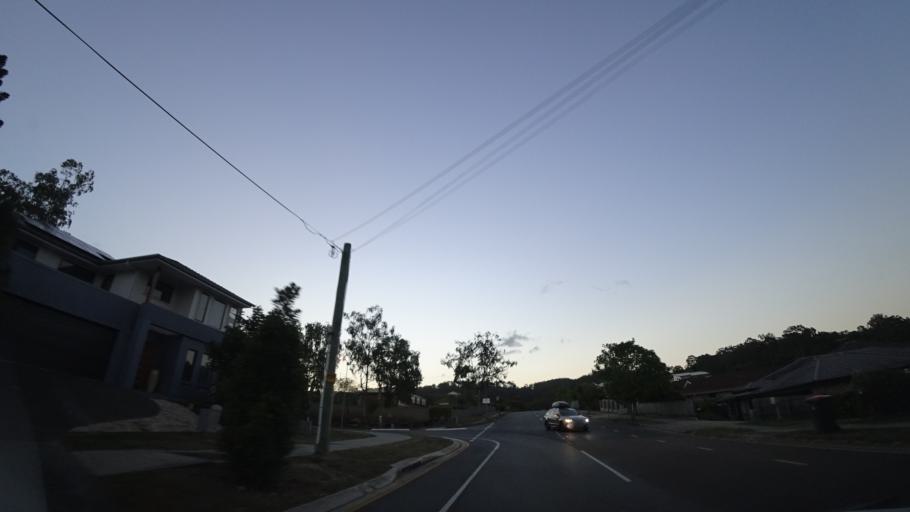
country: AU
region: Queensland
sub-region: Moreton Bay
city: Ferny Hills
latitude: -27.4047
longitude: 152.9261
